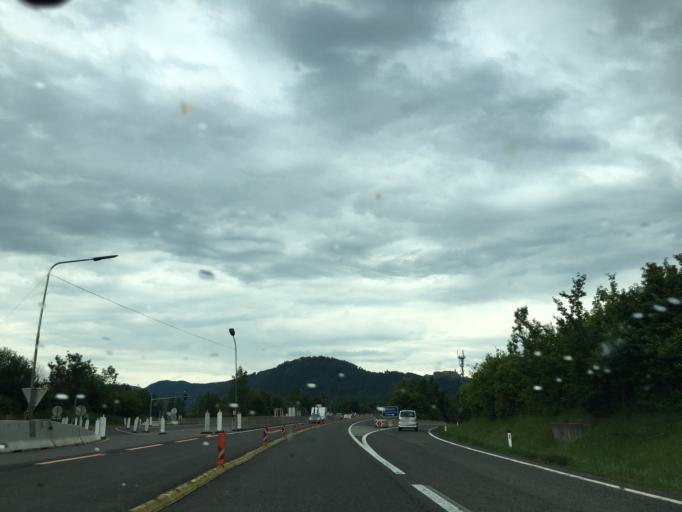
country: AT
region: Carinthia
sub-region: Villach Stadt
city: Villach
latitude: 46.6515
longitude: 13.8678
